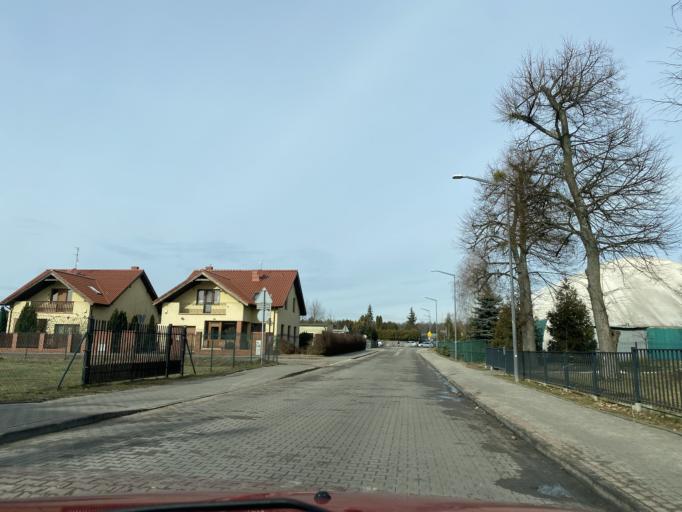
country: PL
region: Greater Poland Voivodeship
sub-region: Powiat poznanski
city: Baranowo
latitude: 52.4367
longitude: 16.8212
